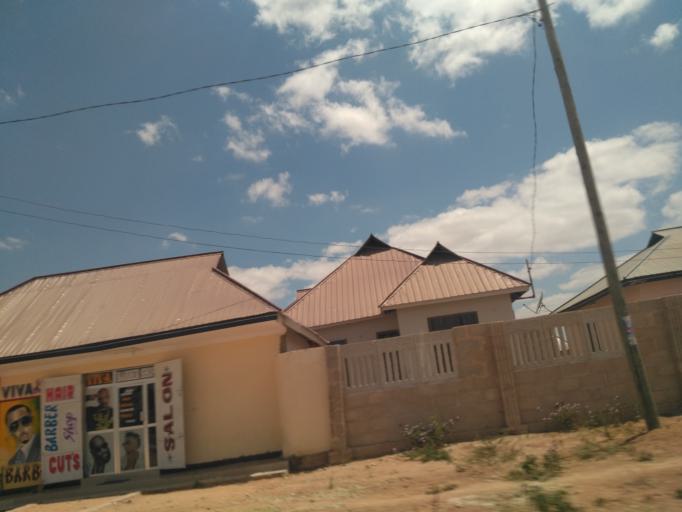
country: TZ
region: Dodoma
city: Kisasa
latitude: -6.1685
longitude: 35.7986
